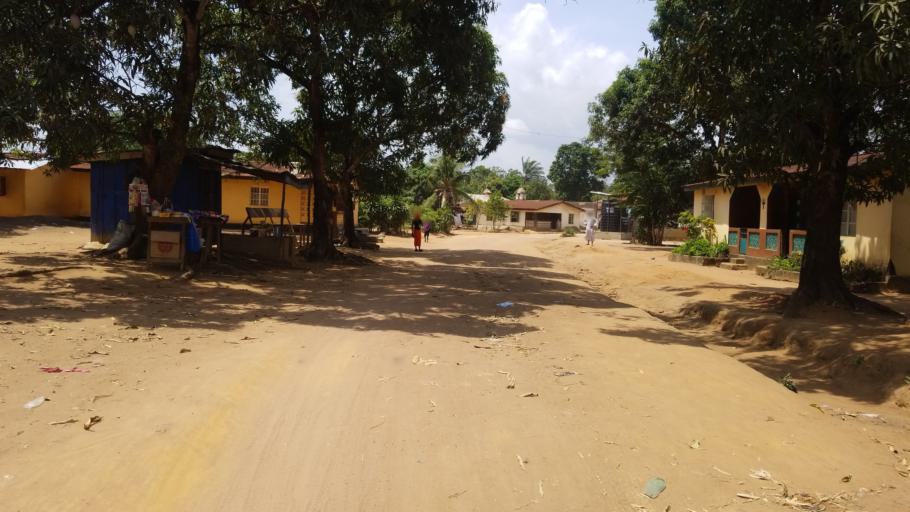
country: SL
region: Western Area
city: Waterloo
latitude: 8.3297
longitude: -13.0611
